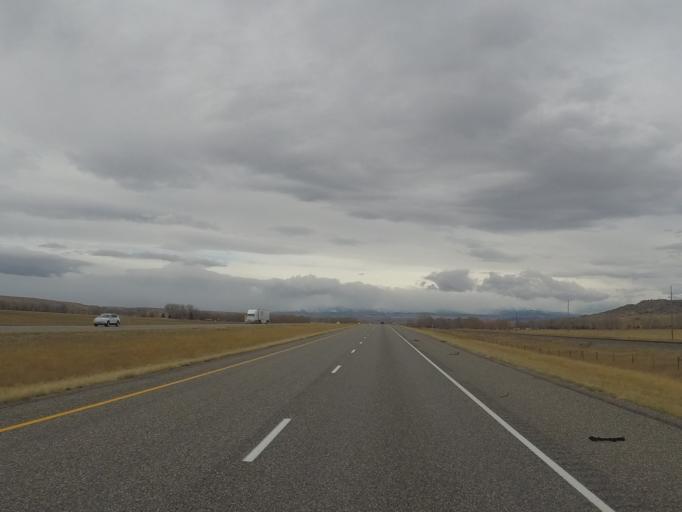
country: US
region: Montana
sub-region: Sweet Grass County
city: Big Timber
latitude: 45.7868
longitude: -109.8191
